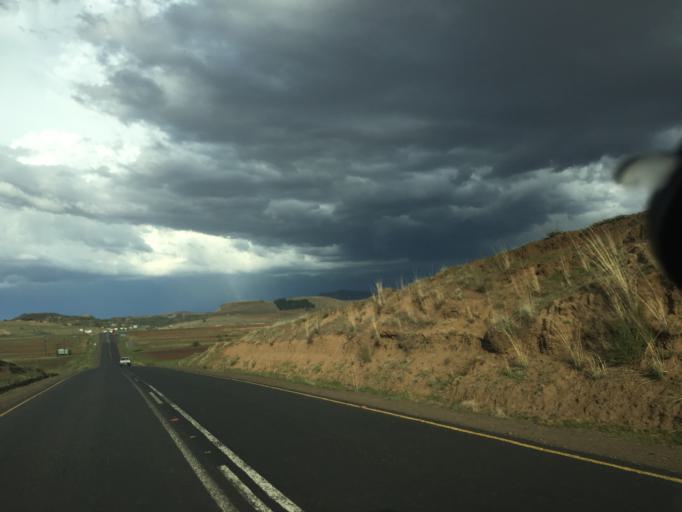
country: LS
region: Berea
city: Teyateyaneng
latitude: -29.0883
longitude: 27.9463
